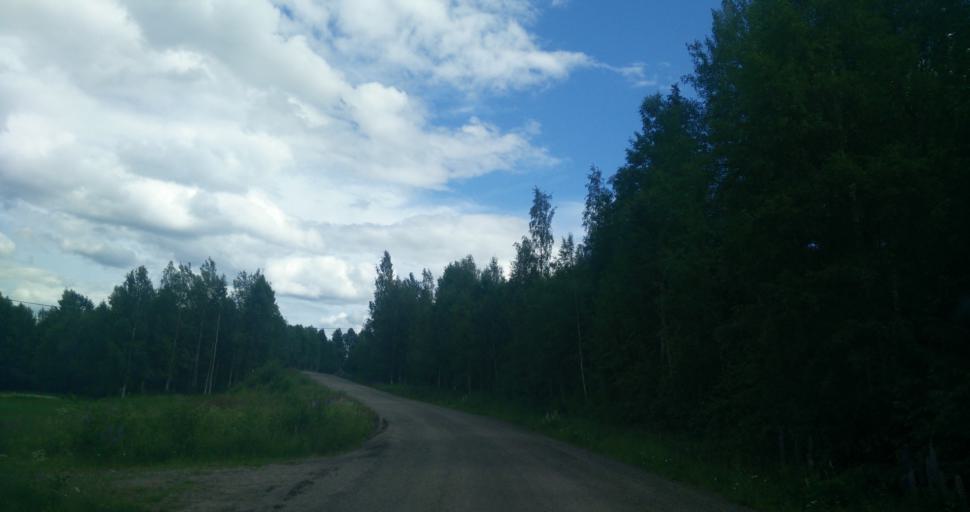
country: SE
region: Gaevleborg
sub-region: Nordanstigs Kommun
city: Bergsjoe
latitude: 62.0667
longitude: 16.7732
